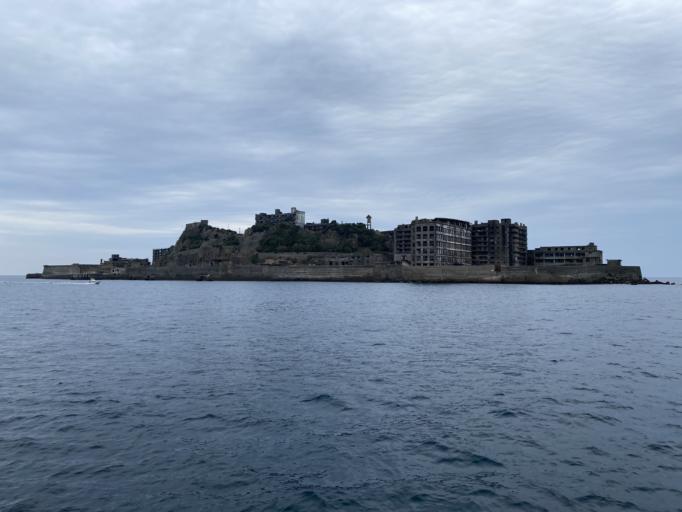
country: JP
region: Nagasaki
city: Nagasaki-shi
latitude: 32.6283
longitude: 129.7423
